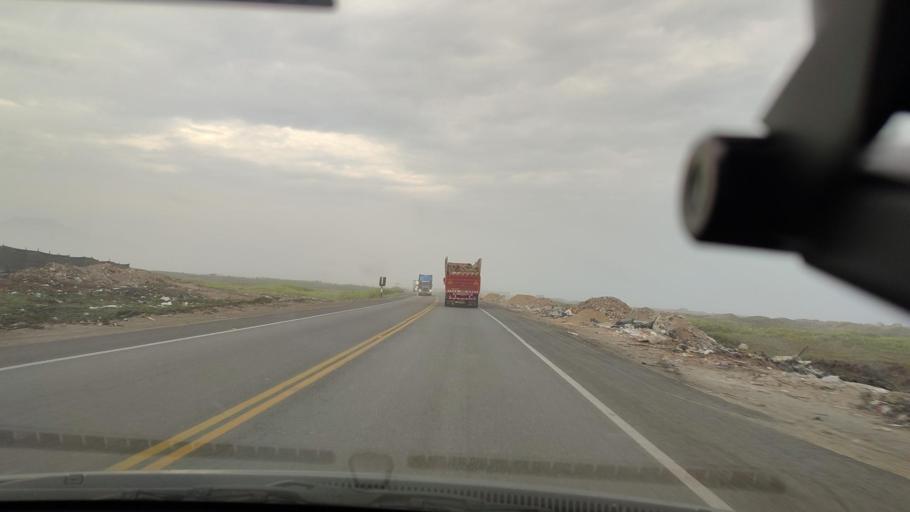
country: PE
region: La Libertad
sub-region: Provincia de Trujillo
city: Huanchaco
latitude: -8.1099
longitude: -79.0962
